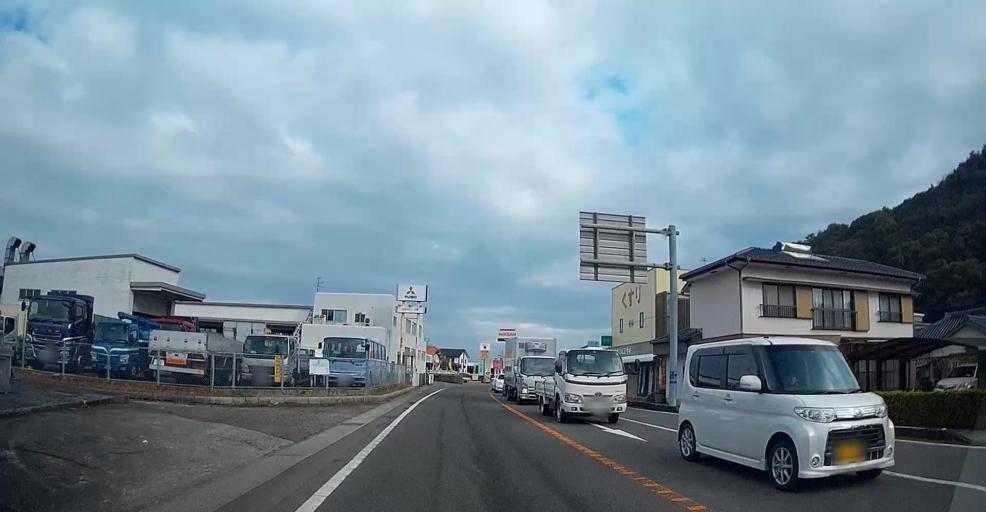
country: JP
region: Kumamoto
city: Hondo
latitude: 32.4483
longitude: 130.2058
